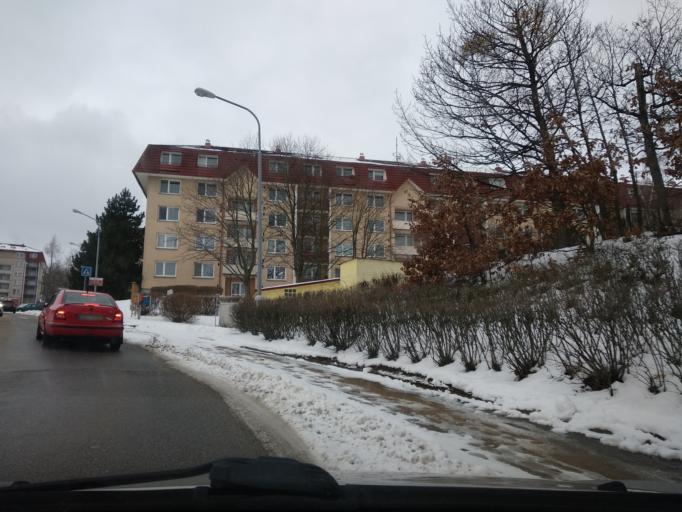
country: CZ
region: South Moravian
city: Troubsko
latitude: 49.1932
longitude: 16.5298
